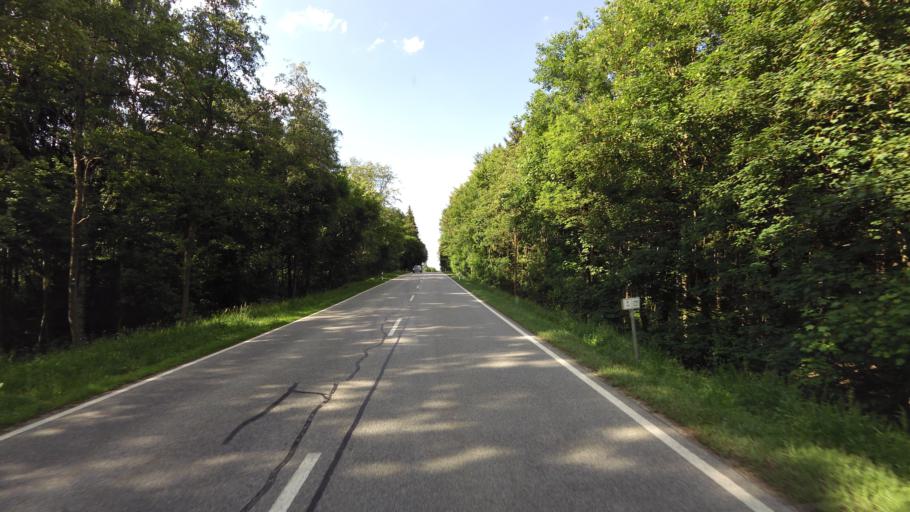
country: DE
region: Bavaria
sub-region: Upper Bavaria
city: Hohenpolding
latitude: 48.4164
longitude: 12.1283
